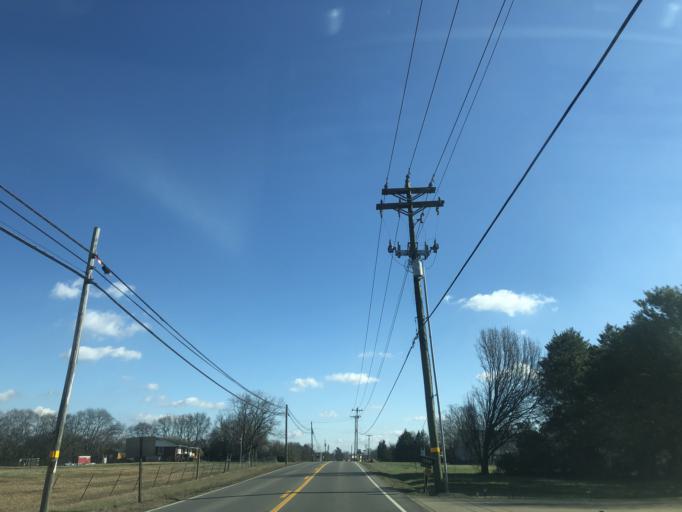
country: US
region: Tennessee
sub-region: Rutherford County
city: Smyrna
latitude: 35.9754
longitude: -86.4031
